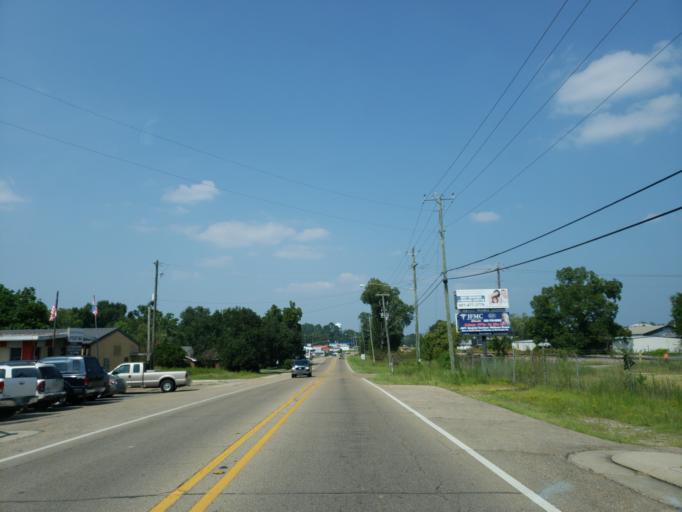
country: US
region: Mississippi
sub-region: Jones County
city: Ellisville
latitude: 31.6015
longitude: -89.2004
